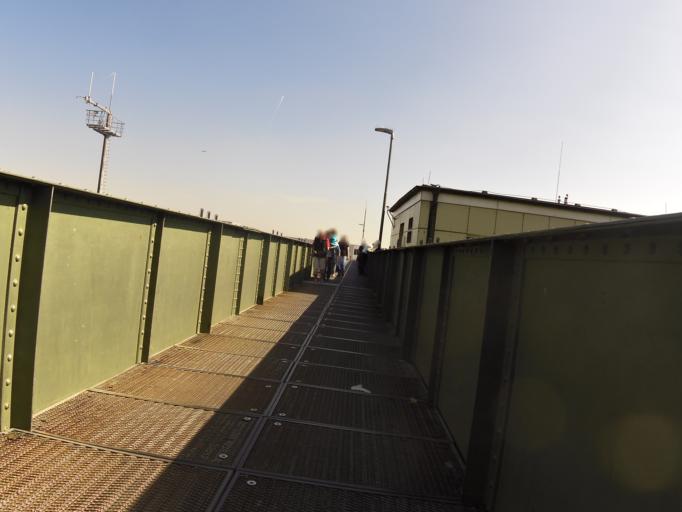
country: DE
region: Hesse
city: Raunheim
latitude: 50.0387
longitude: 8.4773
